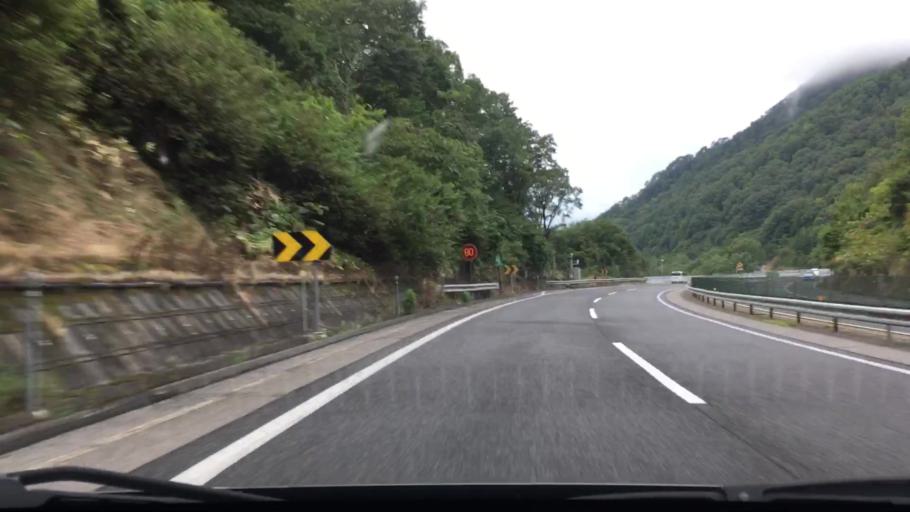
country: JP
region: Hiroshima
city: Miyoshi
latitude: 34.6907
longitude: 132.5875
